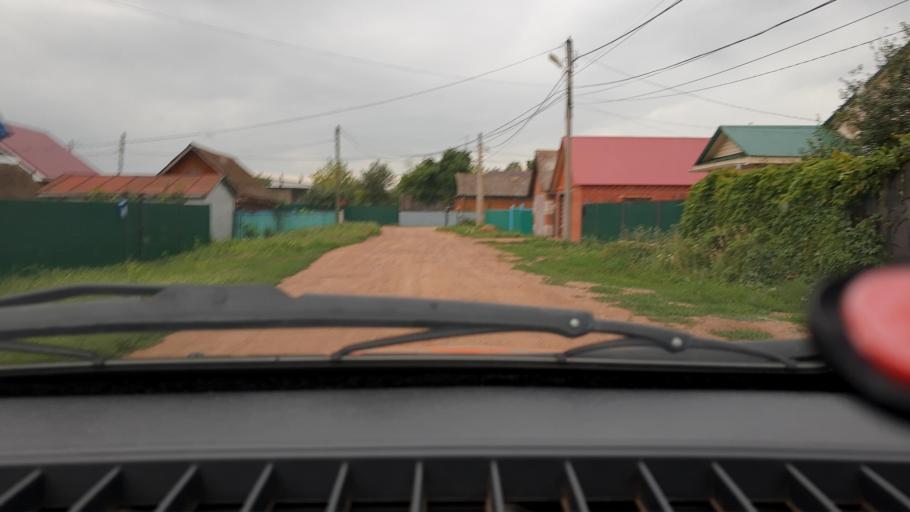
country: RU
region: Bashkortostan
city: Chishmy
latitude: 54.5930
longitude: 55.4055
